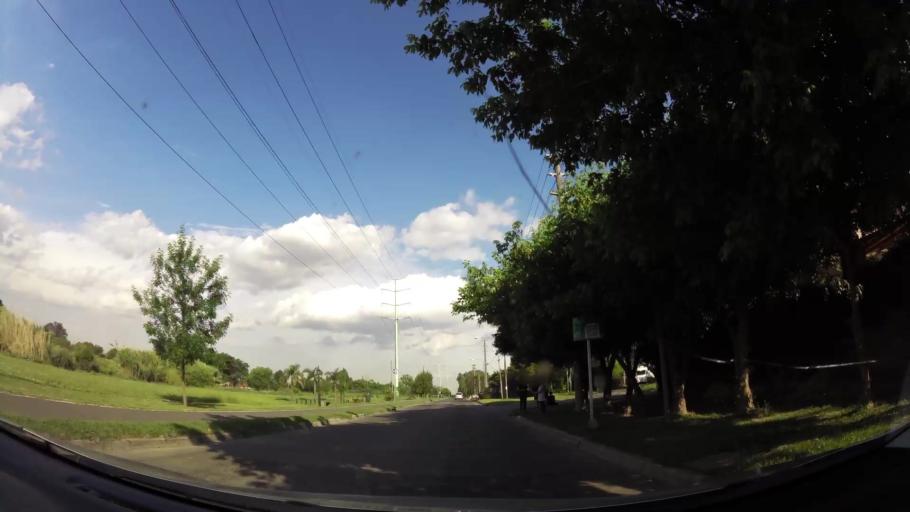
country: AR
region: Buenos Aires
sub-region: Partido de Tigre
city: Tigre
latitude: -34.4665
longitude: -58.6380
